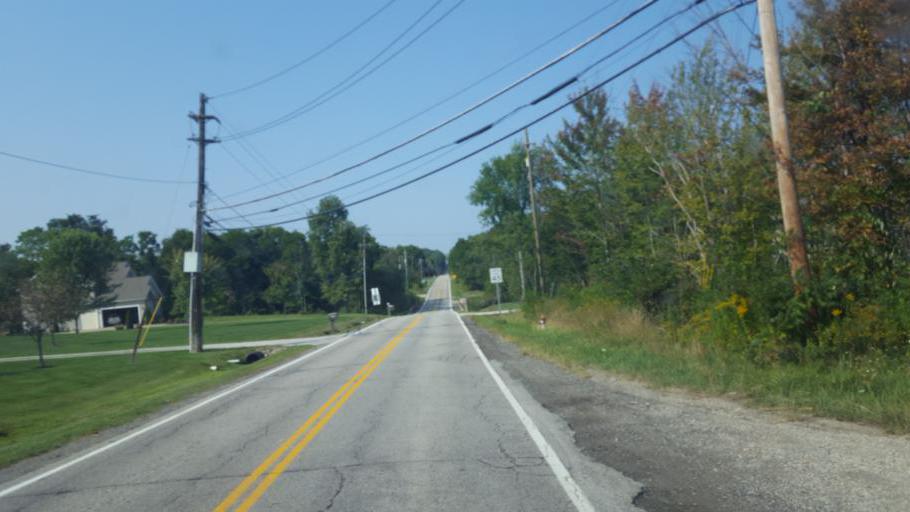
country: US
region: Ohio
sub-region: Geauga County
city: Chardon
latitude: 41.6615
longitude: -81.1968
